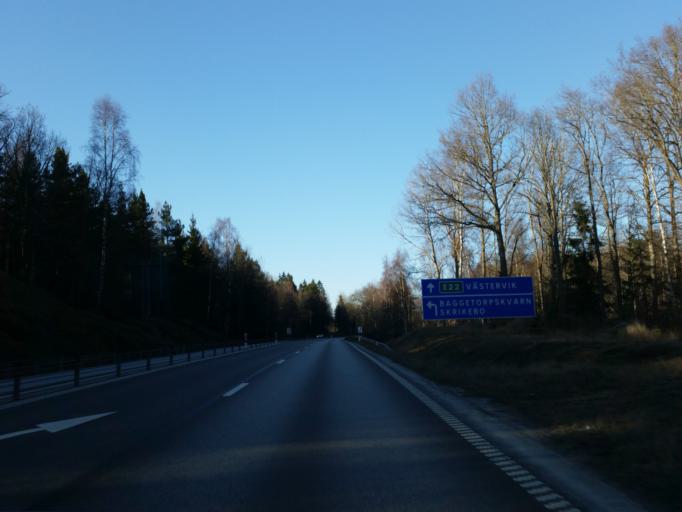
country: SE
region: Kalmar
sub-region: Oskarshamns Kommun
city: Oskarshamn
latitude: 57.3086
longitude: 16.4621
